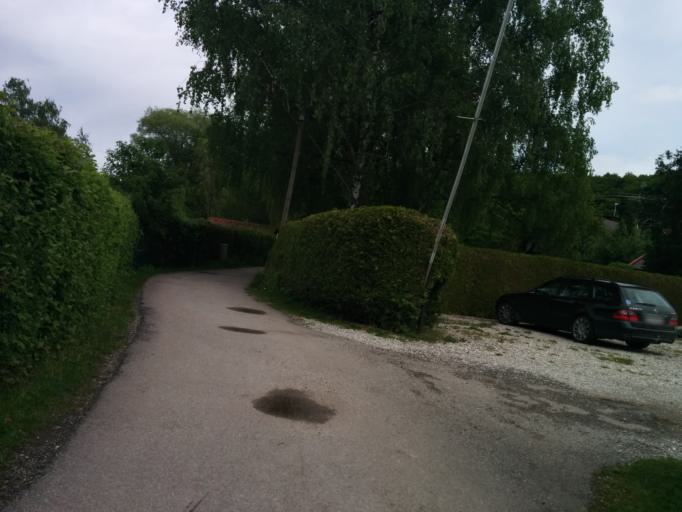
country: DE
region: Bavaria
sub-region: Upper Bavaria
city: Worthsee
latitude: 48.0665
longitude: 11.1994
